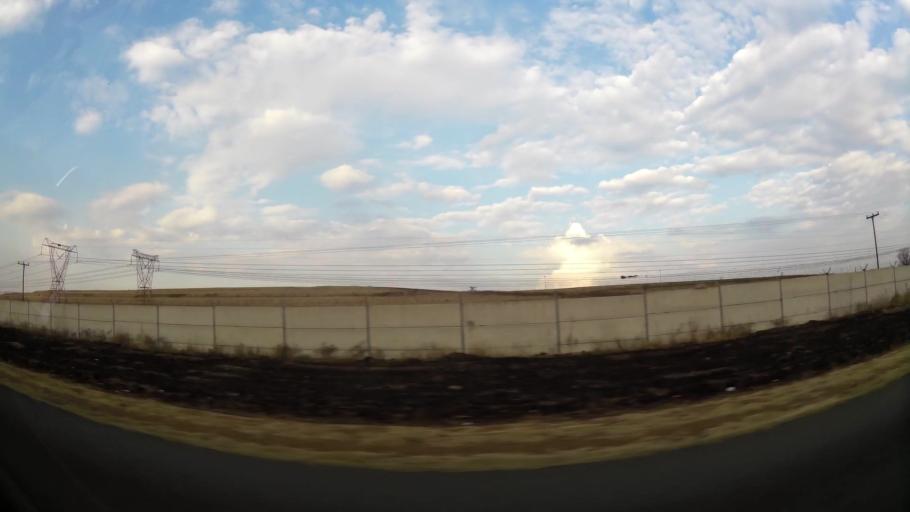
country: ZA
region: Gauteng
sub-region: Sedibeng District Municipality
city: Vanderbijlpark
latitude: -26.6395
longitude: 27.8061
